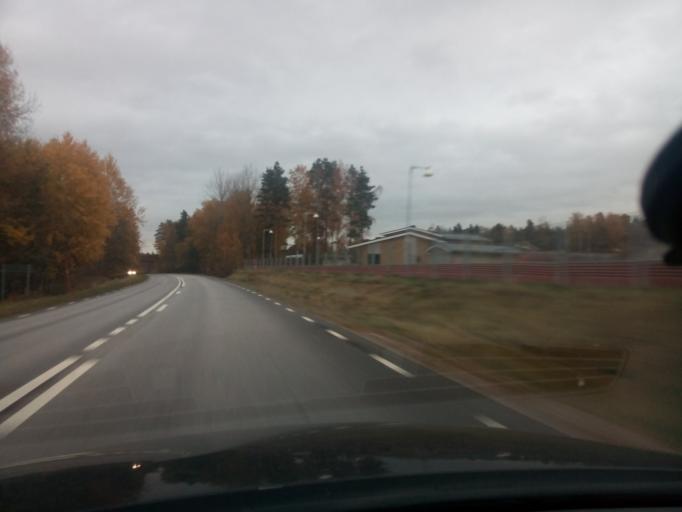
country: SE
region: Soedermanland
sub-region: Nykopings Kommun
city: Nykoping
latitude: 58.7599
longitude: 17.0491
